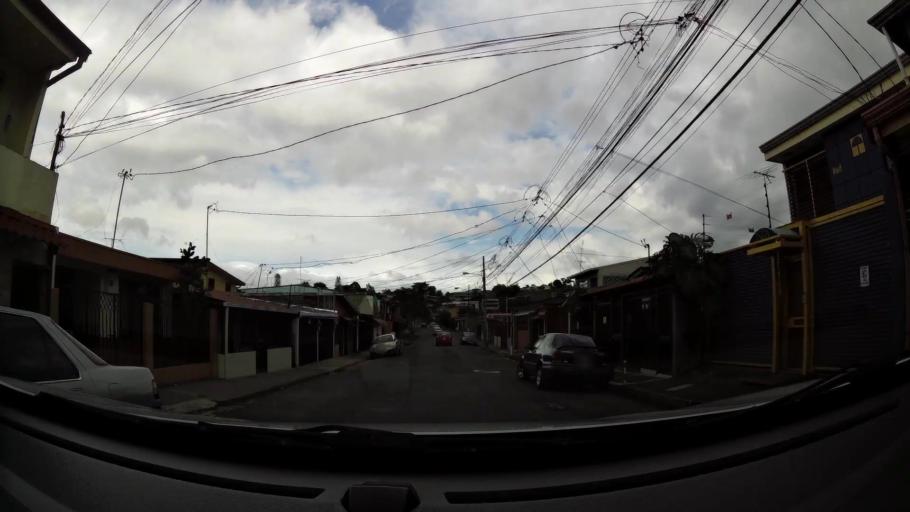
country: CR
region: San Jose
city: San Pedro
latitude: 9.9239
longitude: -84.0513
